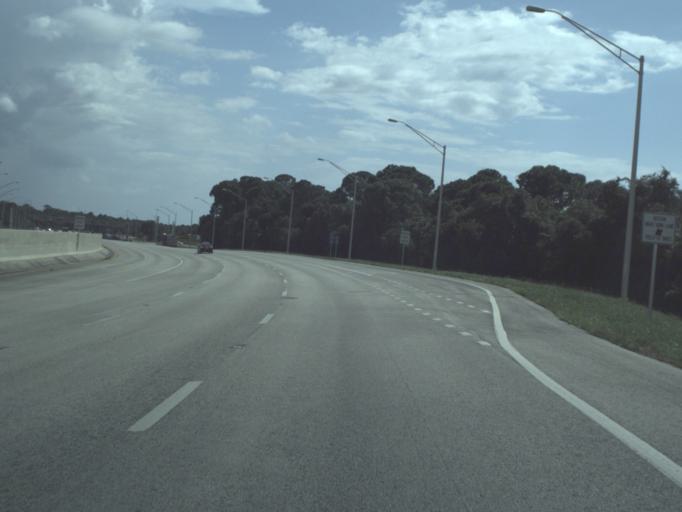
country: US
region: Florida
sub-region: Sarasota County
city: North Sarasota
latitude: 27.3923
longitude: -82.5331
